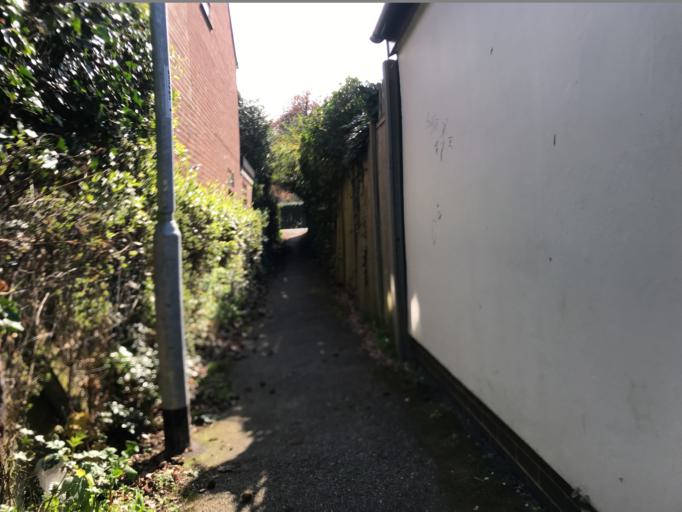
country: GB
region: England
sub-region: Cambridgeshire
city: Sawston
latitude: 52.1533
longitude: 0.1451
